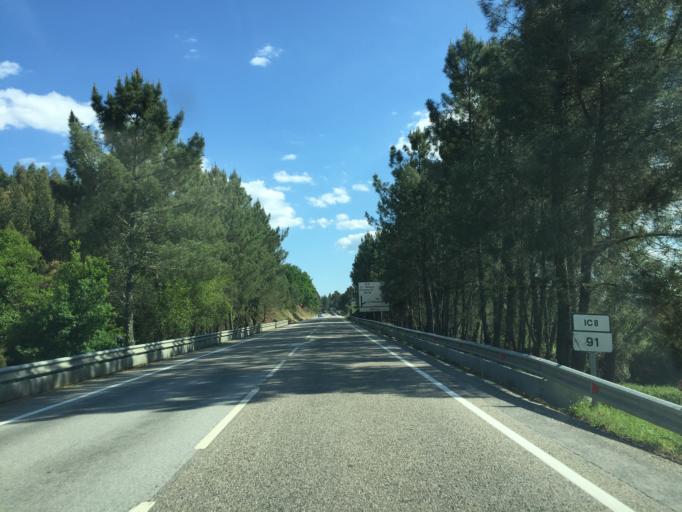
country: PT
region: Leiria
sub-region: Pedrogao Grande
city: Pedrogao Grande
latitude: 39.9170
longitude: -8.1538
